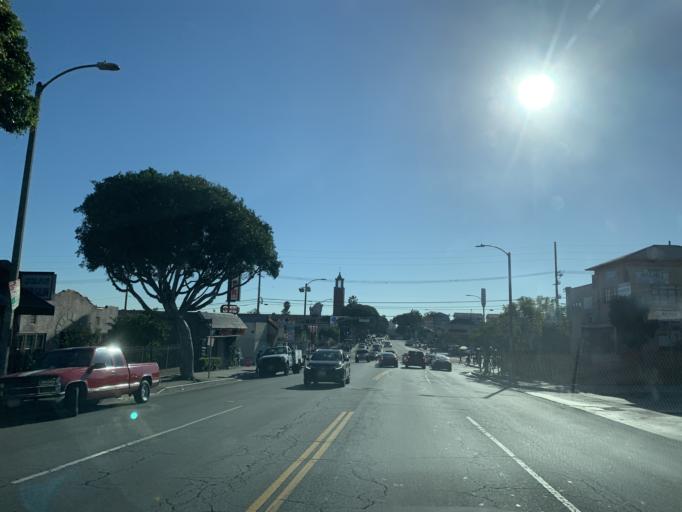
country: US
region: California
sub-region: Los Angeles County
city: Boyle Heights
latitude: 34.0358
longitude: -118.2151
